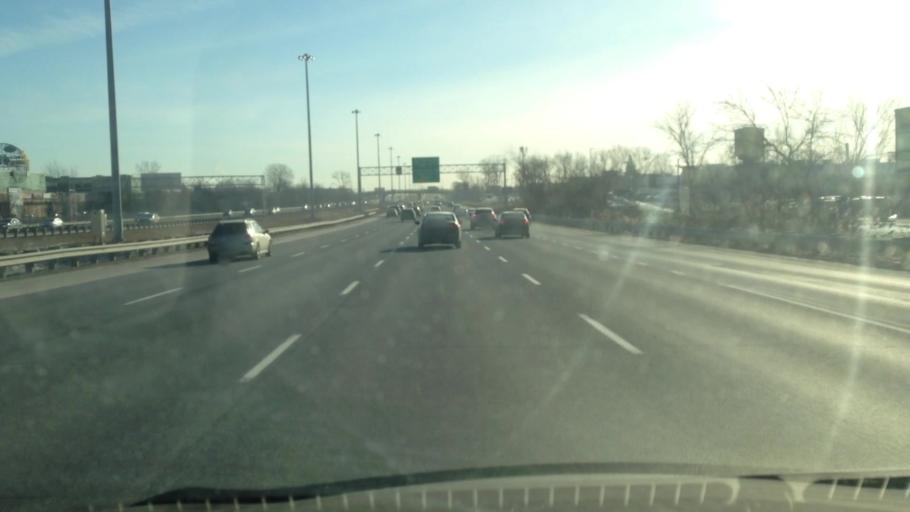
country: CA
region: Quebec
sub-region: Laurentides
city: Blainville
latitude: 45.6436
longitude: -73.8645
